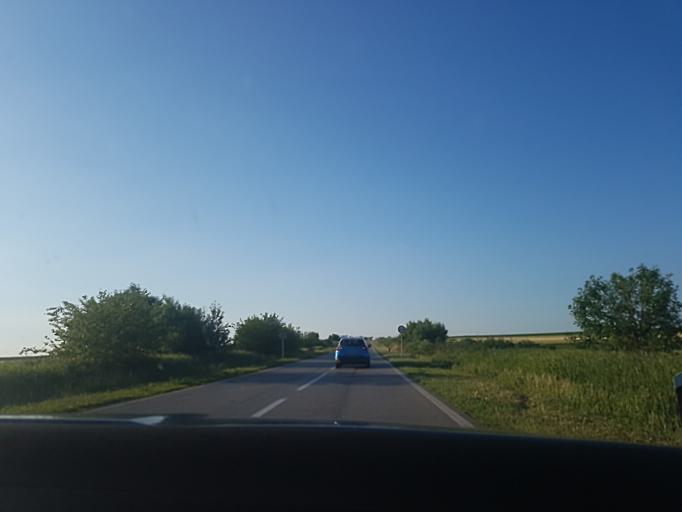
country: RS
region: Autonomna Pokrajina Vojvodina
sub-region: Juznobanatski Okrug
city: Vrsac
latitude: 45.1557
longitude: 21.2905
